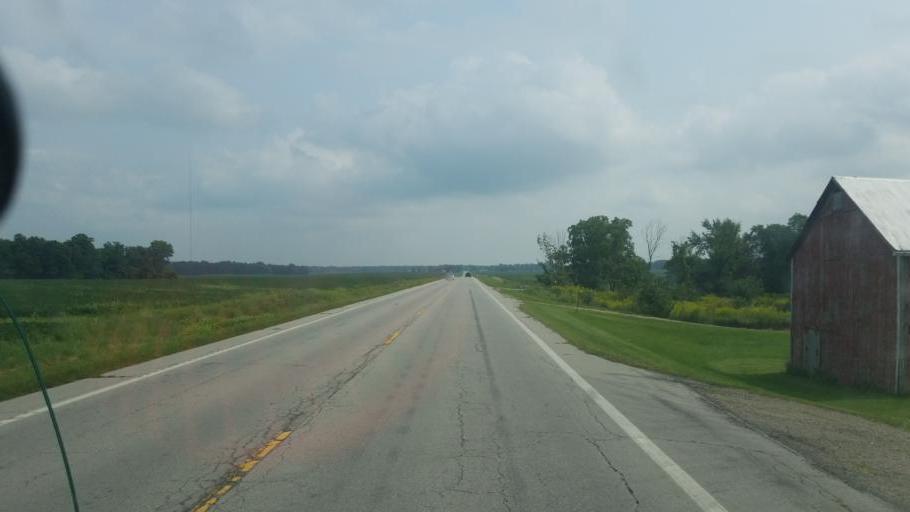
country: US
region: Ohio
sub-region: Huron County
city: Greenwich
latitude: 41.0835
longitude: -82.4714
